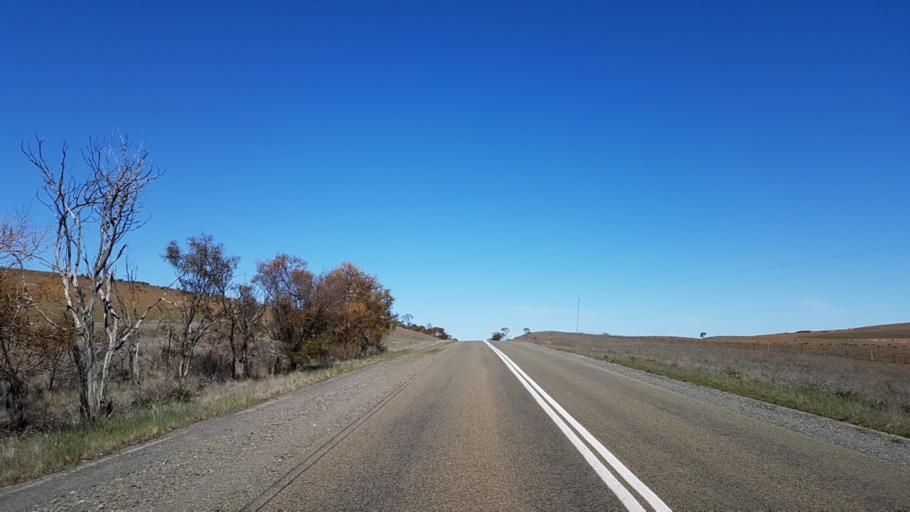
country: AU
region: South Australia
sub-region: Peterborough
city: Peterborough
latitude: -33.0489
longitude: 138.8664
